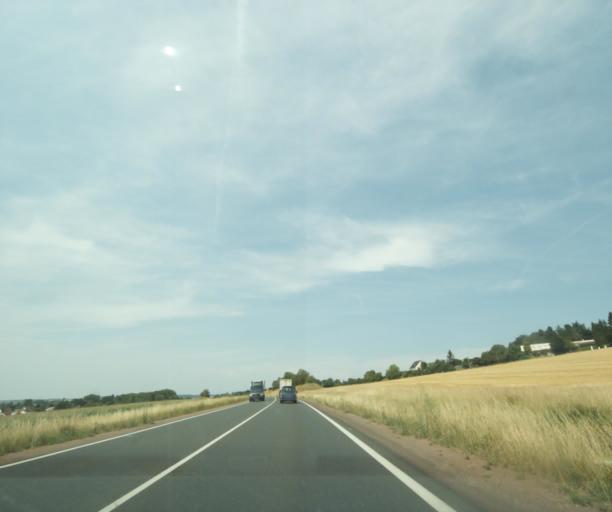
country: FR
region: Poitou-Charentes
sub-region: Departement de la Vienne
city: Chatellerault
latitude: 46.8119
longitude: 0.5676
